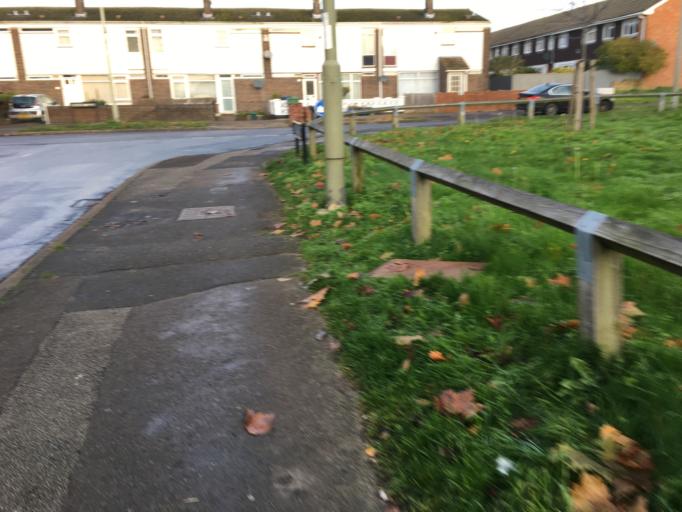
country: GB
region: England
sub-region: Oxfordshire
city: Cowley
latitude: 51.7237
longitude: -1.1942
